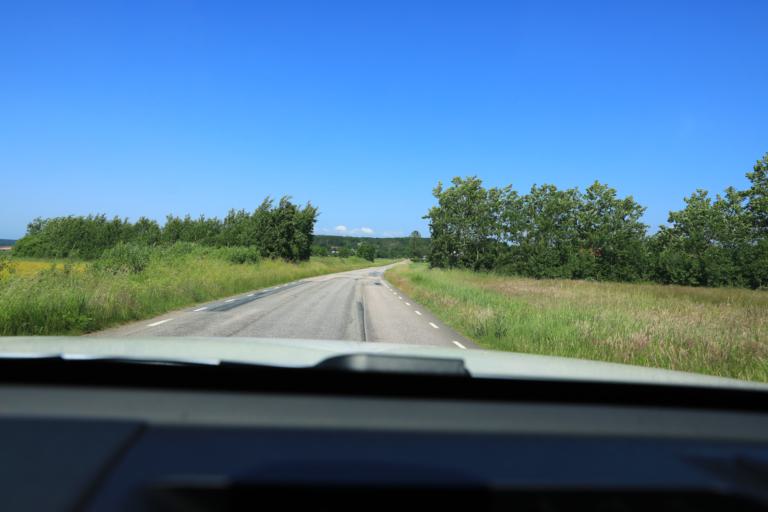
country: SE
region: Halland
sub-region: Varbergs Kommun
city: Varberg
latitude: 57.1619
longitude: 12.3148
